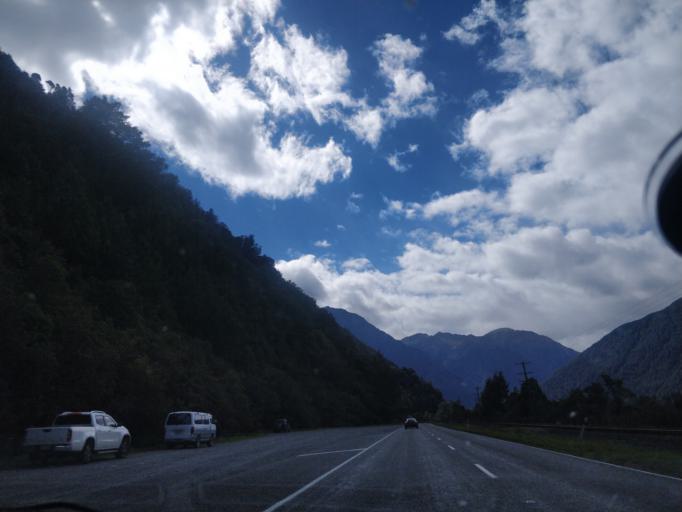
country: NZ
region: West Coast
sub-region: Grey District
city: Greymouth
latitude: -42.7871
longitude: 171.6032
